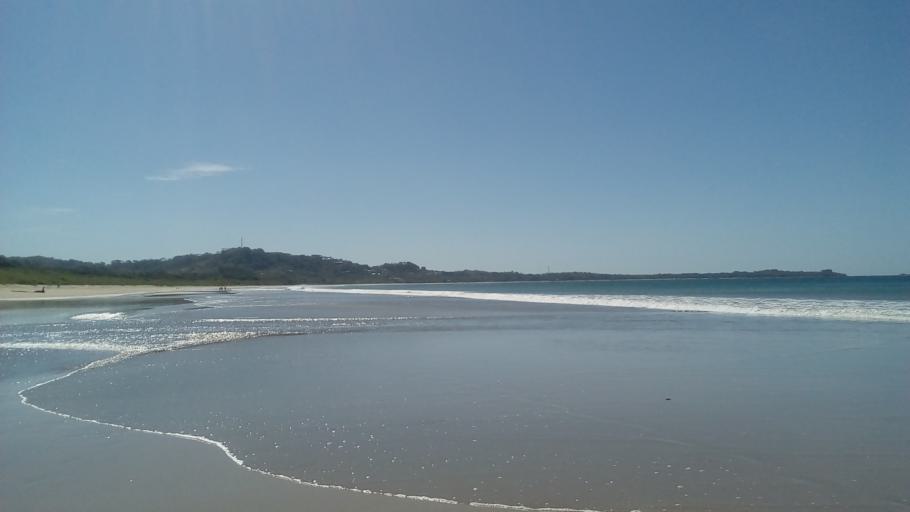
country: CR
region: Guanacaste
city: Belen
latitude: 10.3292
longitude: -85.8454
